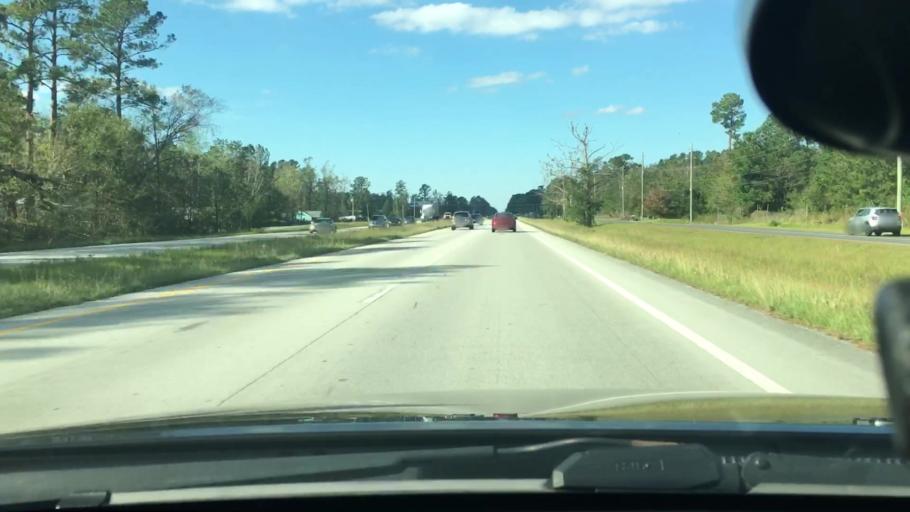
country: US
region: North Carolina
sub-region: Craven County
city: Neuse Forest
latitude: 35.0054
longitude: -76.9893
